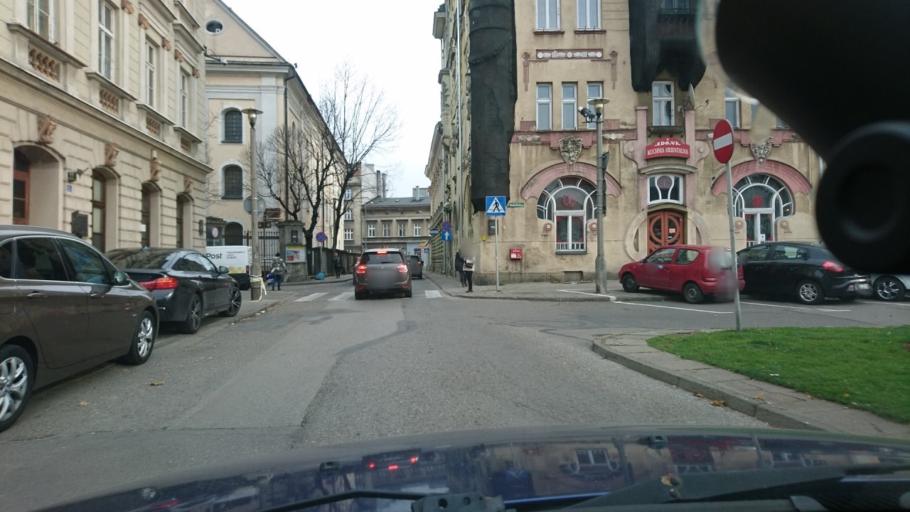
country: PL
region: Silesian Voivodeship
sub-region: Bielsko-Biala
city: Bielsko-Biala
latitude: 49.8238
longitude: 19.0511
